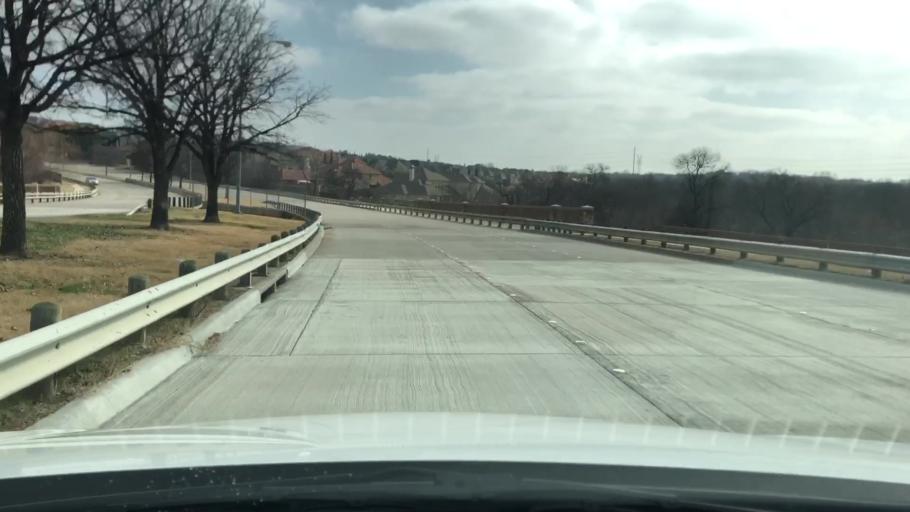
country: US
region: Texas
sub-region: Denton County
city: The Colony
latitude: 33.0706
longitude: -96.8502
